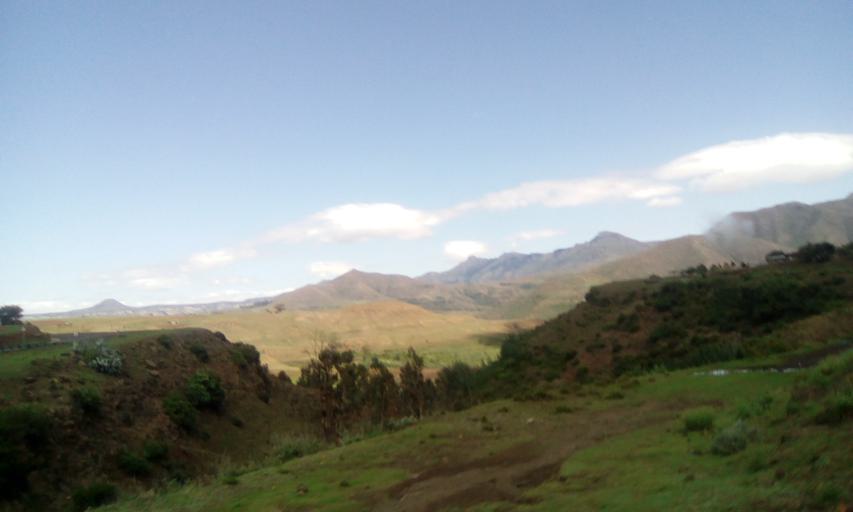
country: LS
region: Maseru
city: Nako
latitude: -29.6408
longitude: 27.7654
